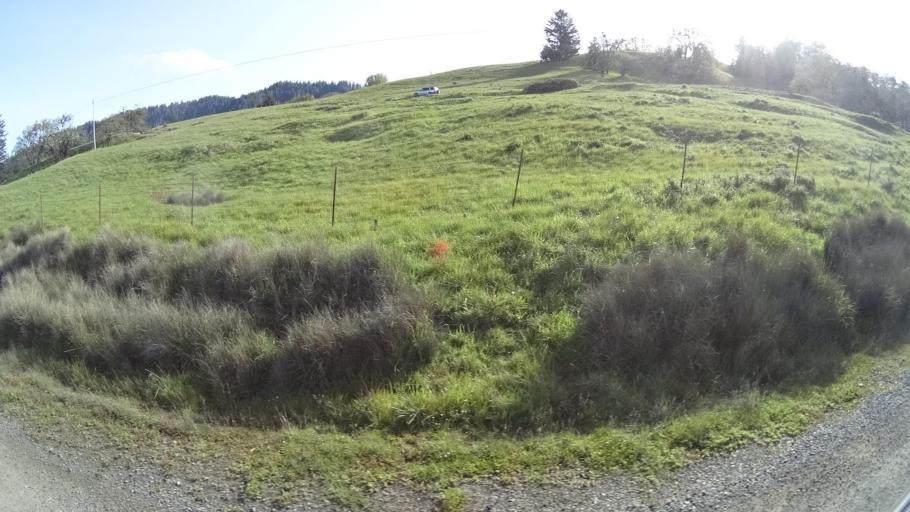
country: US
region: California
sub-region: Humboldt County
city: Hydesville
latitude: 40.6583
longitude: -123.9263
